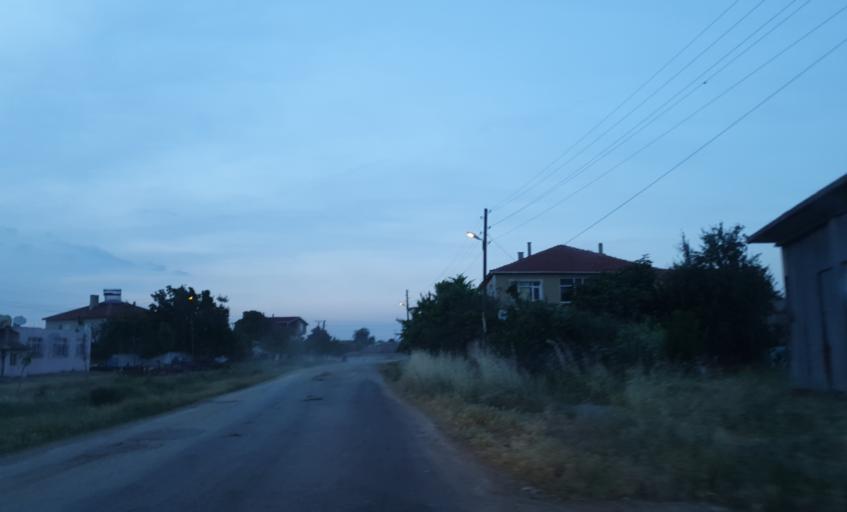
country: TR
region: Kirklareli
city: Vize
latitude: 41.4837
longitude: 27.7526
